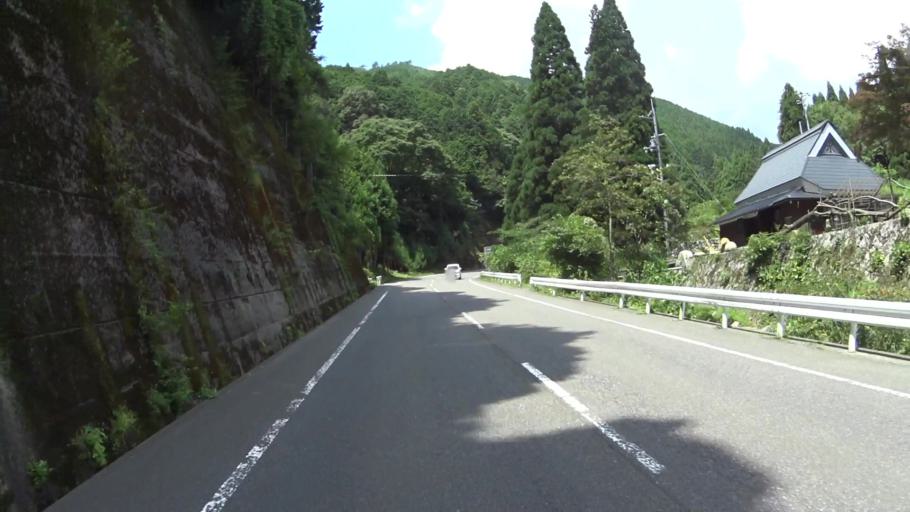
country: JP
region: Shiga Prefecture
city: Kitahama
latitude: 35.1730
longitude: 135.8581
